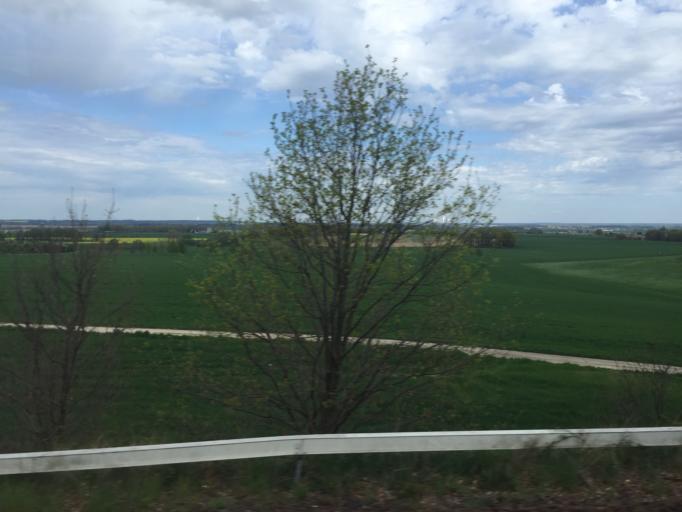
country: DE
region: Saxony
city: Kubschutz
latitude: 51.1666
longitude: 14.5156
